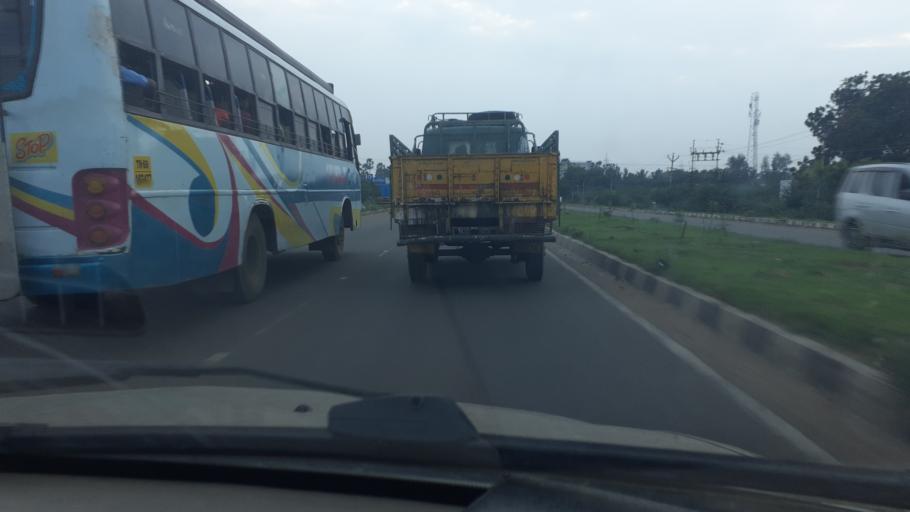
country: IN
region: Tamil Nadu
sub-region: Thoothukkudi
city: Korampallam
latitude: 8.7756
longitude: 78.0885
